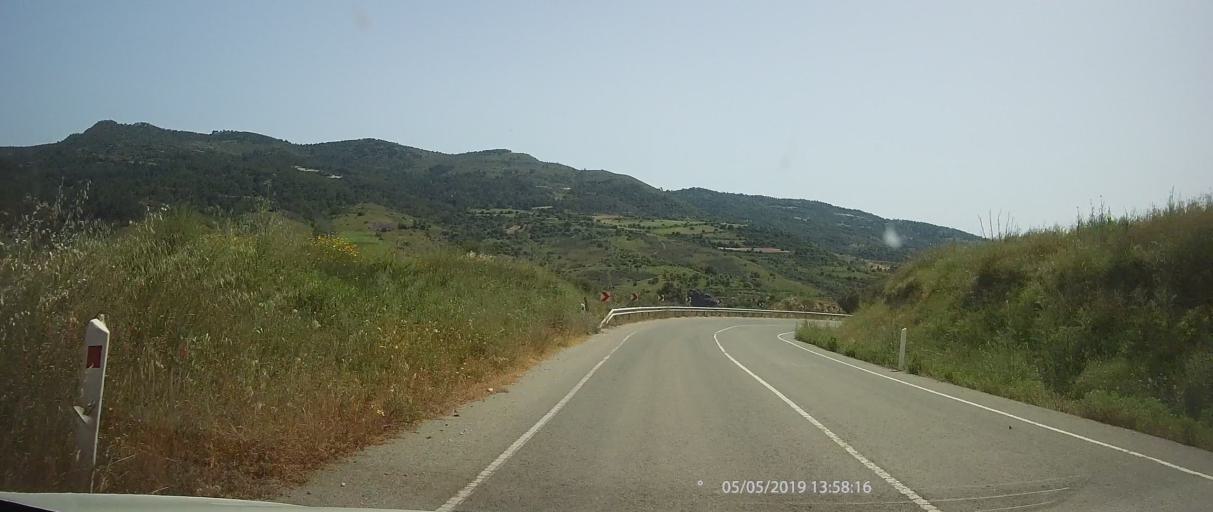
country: CY
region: Limassol
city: Pachna
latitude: 34.7906
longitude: 32.6922
